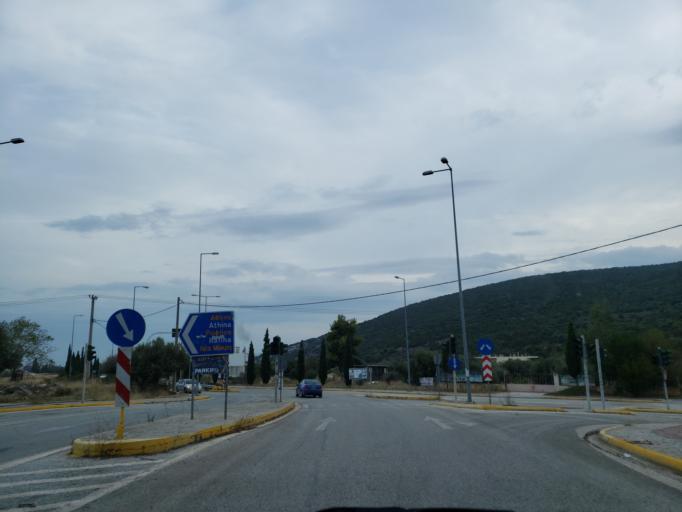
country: GR
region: Attica
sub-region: Nomarchia Anatolikis Attikis
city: Marathonas
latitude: 38.1495
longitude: 23.9639
